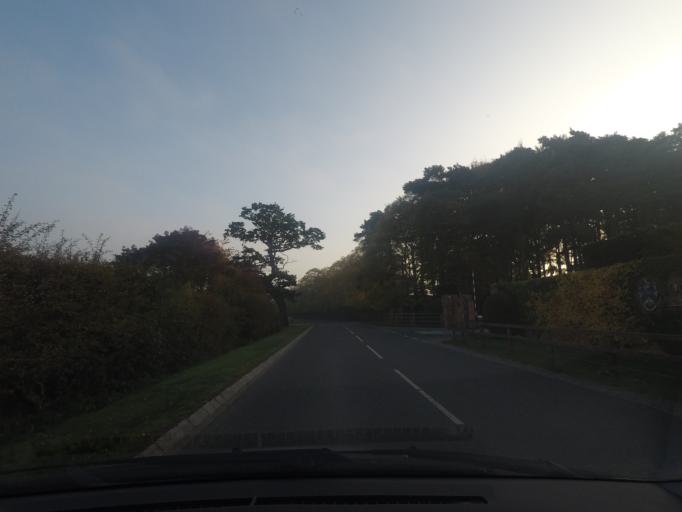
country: GB
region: England
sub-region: City and Borough of Leeds
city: Walton
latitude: 54.0271
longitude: -1.2972
